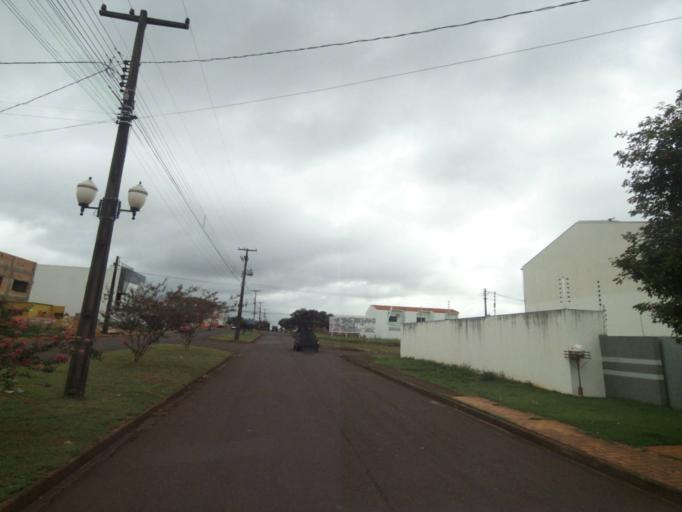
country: BR
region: Parana
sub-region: Campo Mourao
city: Campo Mourao
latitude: -24.0281
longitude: -52.3579
